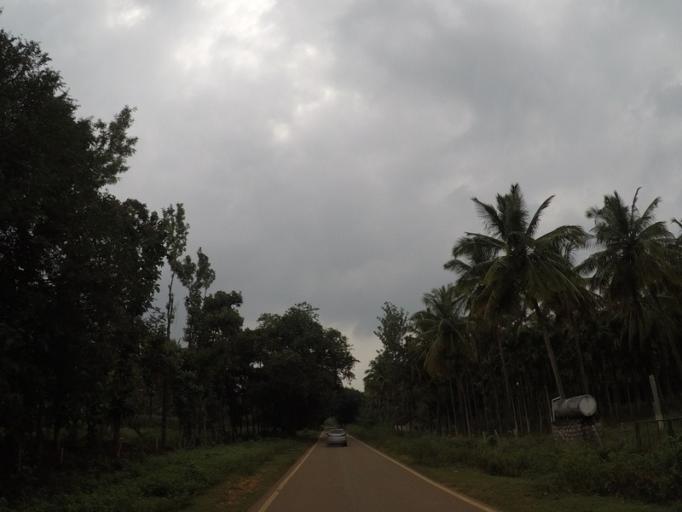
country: IN
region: Karnataka
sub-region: Chikmagalur
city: Tarikere
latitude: 13.5905
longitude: 75.8378
